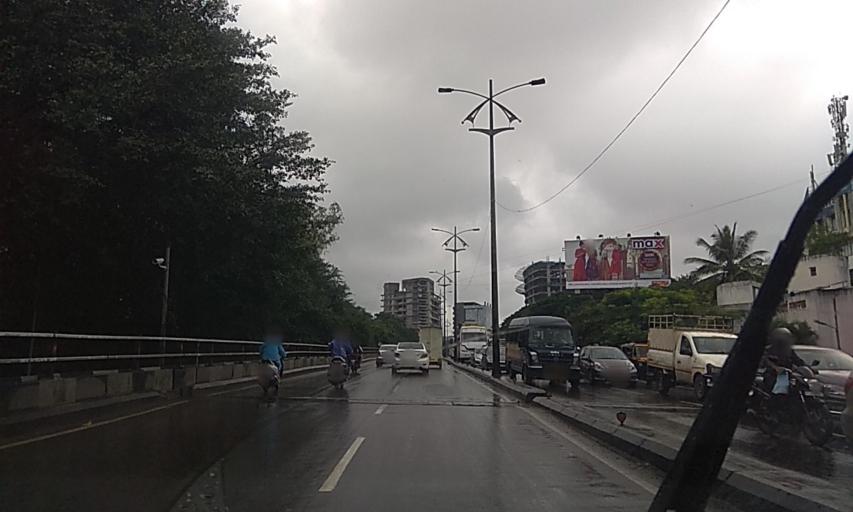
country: IN
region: Maharashtra
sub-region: Pune Division
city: Shivaji Nagar
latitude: 18.5311
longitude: 73.8460
